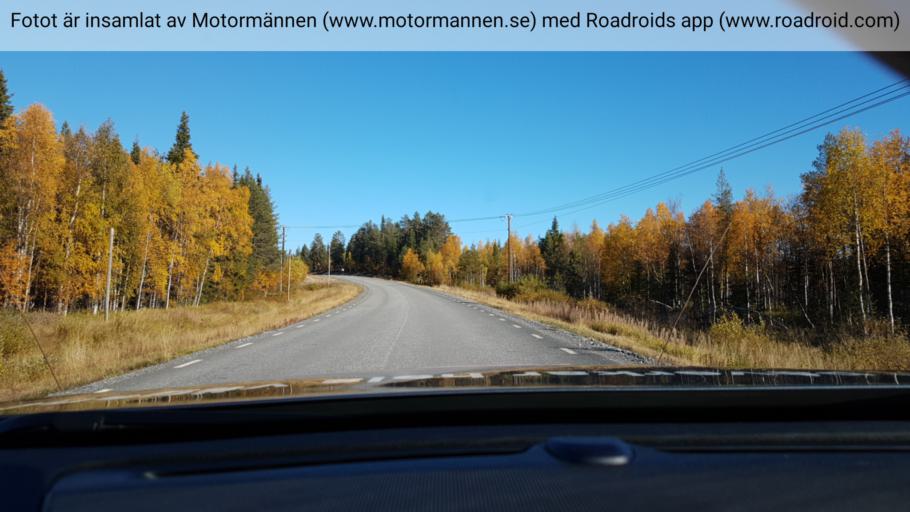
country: SE
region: Norrbotten
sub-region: Gallivare Kommun
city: Gaellivare
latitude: 66.7686
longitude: 21.0462
